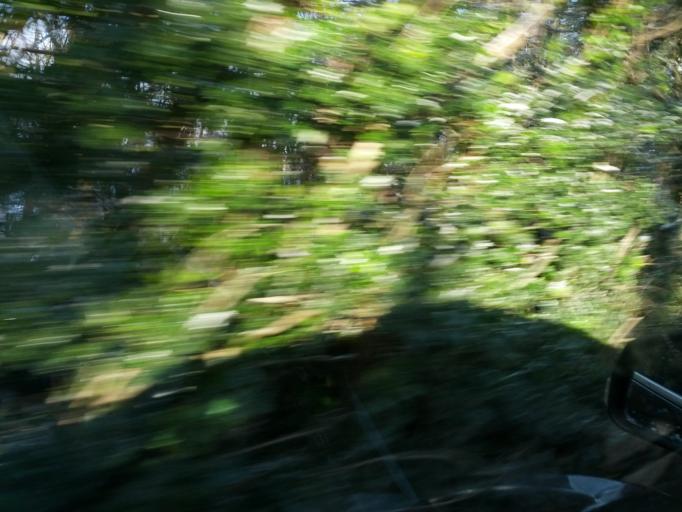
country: IE
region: Connaught
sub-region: County Galway
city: Gort
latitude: 53.1850
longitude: -8.8195
